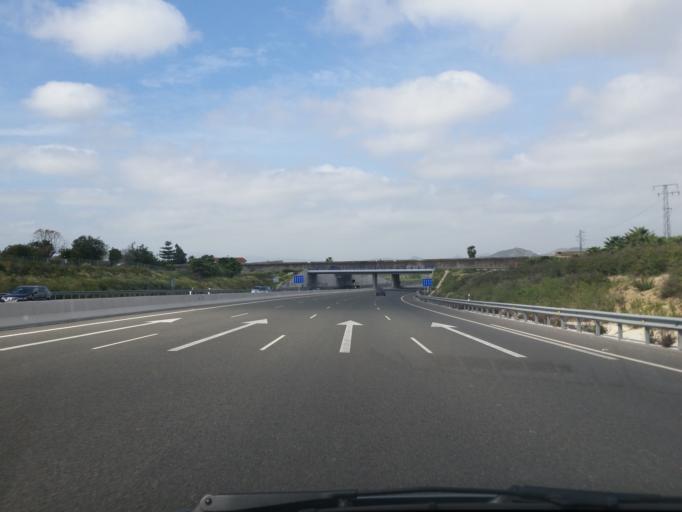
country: ES
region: Andalusia
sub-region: Provincia de Malaga
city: Alhaurin de la Torre
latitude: 36.6847
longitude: -4.5265
